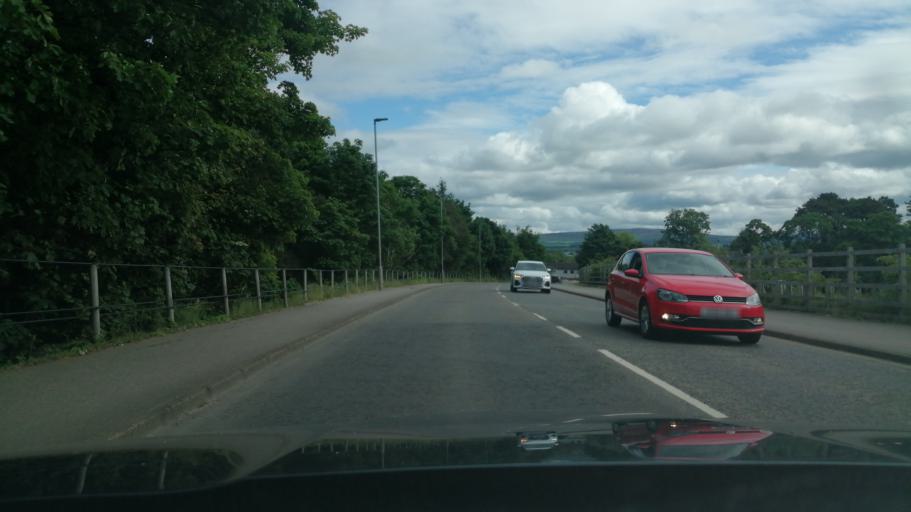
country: GB
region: Scotland
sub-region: Moray
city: Elgin
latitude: 57.6561
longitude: -3.3024
